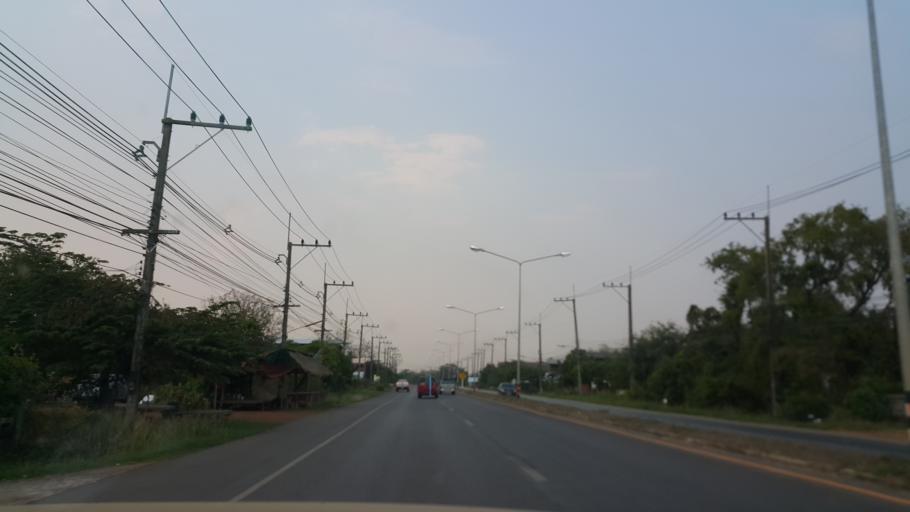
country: TH
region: Nakhon Phanom
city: That Phanom
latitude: 16.9853
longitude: 104.7275
